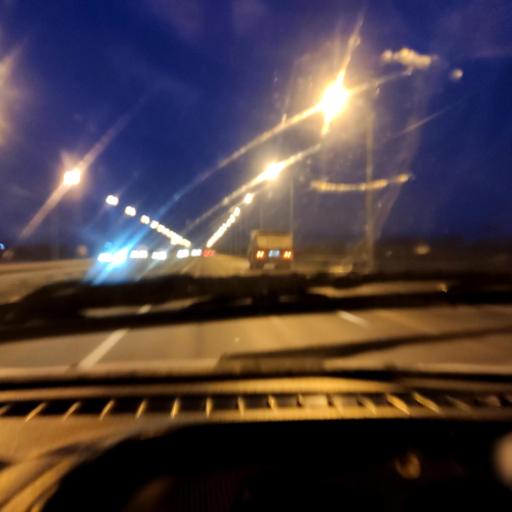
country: RU
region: Samara
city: Tol'yatti
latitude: 53.5741
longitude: 49.4502
